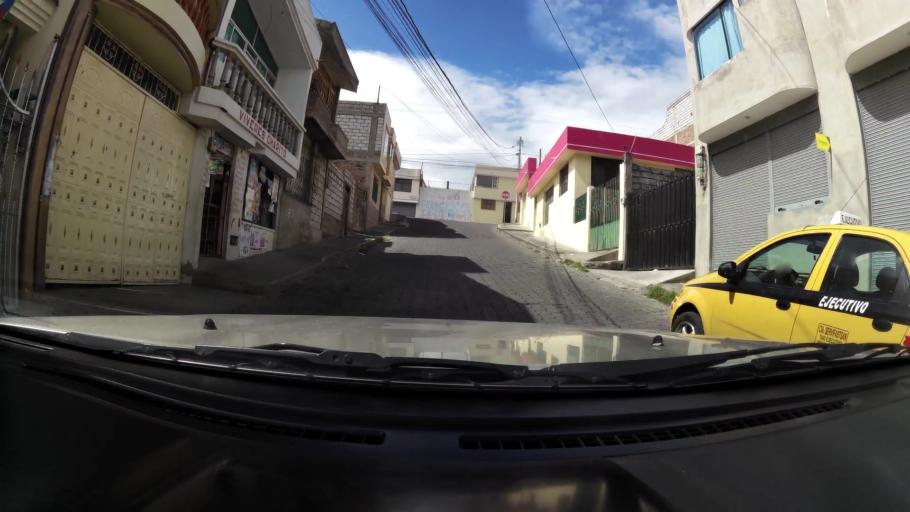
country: EC
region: Cotopaxi
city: Latacunga
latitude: -0.9300
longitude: -78.6023
